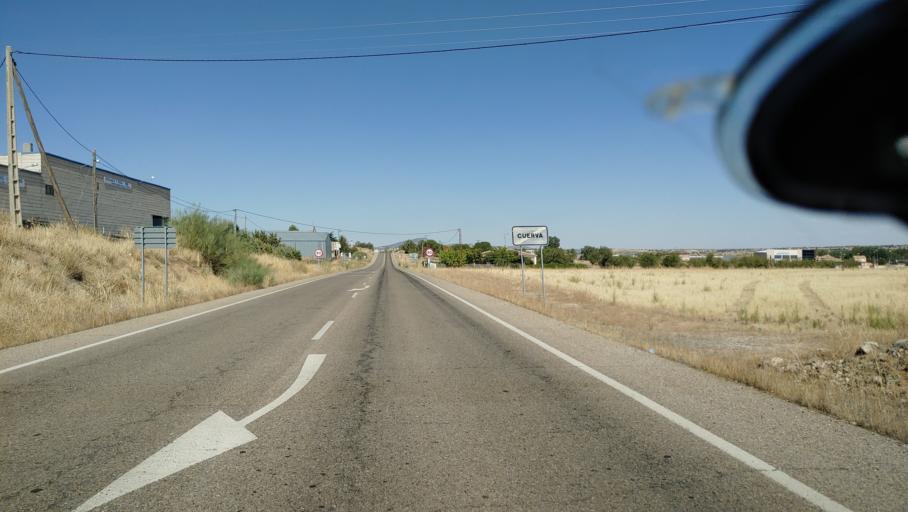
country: ES
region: Castille-La Mancha
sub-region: Province of Toledo
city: Cuerva
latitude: 39.6676
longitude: -4.2030
